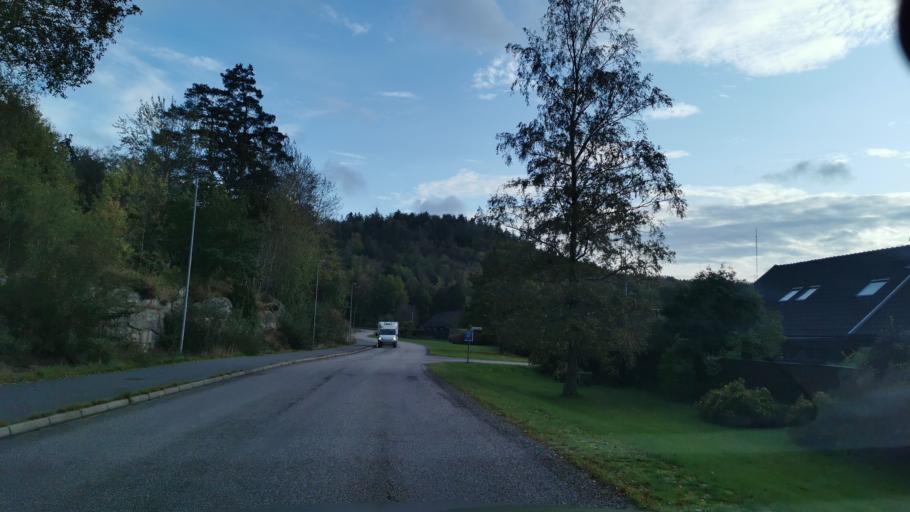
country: SE
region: Vaestra Goetaland
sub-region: Partille Kommun
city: Partille
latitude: 57.7150
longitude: 12.0802
